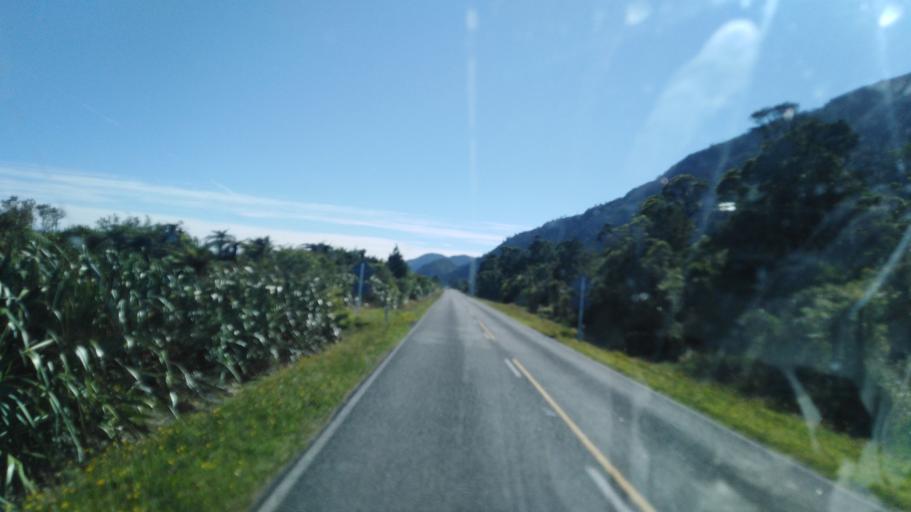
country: NZ
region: West Coast
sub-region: Buller District
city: Westport
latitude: -41.6502
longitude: 171.8315
